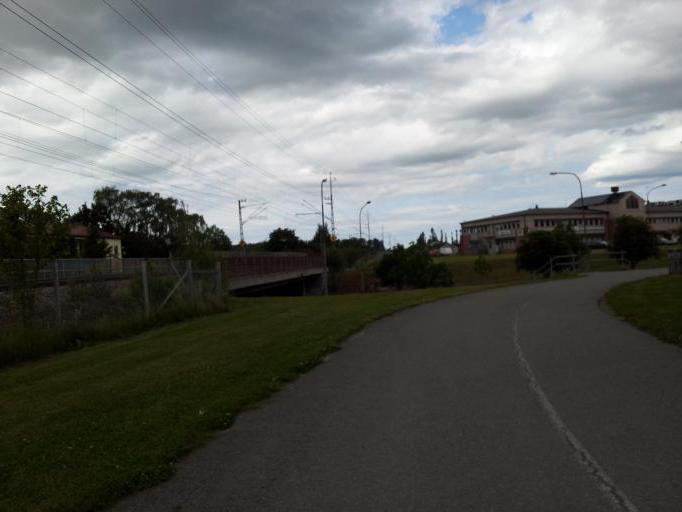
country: SE
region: Uppsala
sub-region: Uppsala Kommun
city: Uppsala
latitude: 59.8722
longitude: 17.6359
